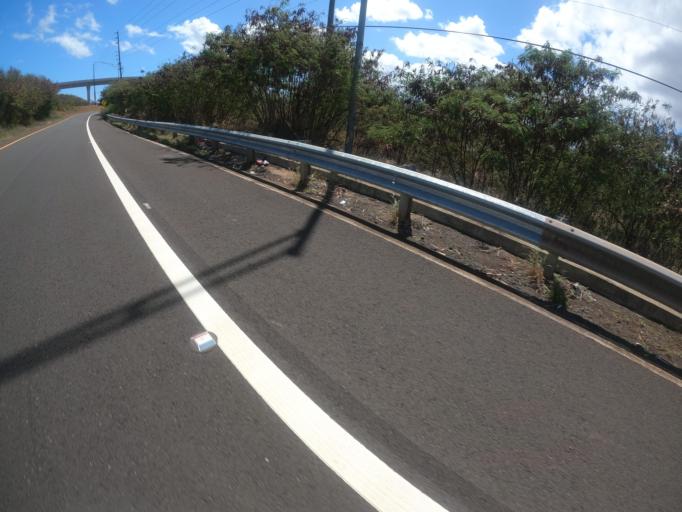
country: US
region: Hawaii
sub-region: Honolulu County
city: Royal Kunia
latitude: 21.3776
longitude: -158.0277
